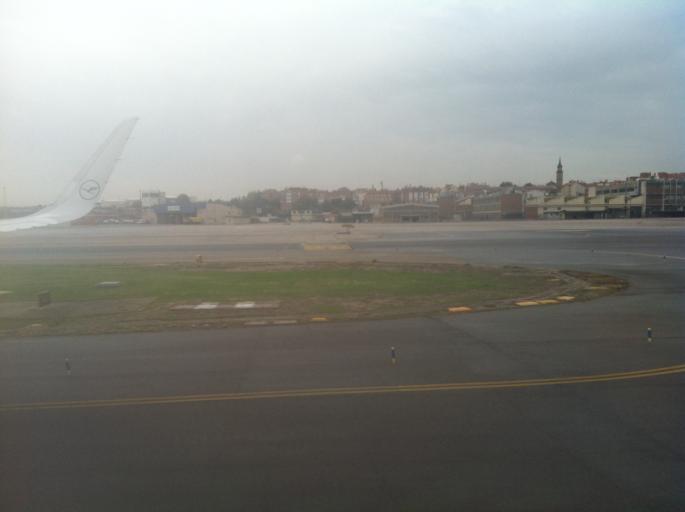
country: ES
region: Madrid
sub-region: Provincia de Madrid
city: Barajas de Madrid
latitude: 40.4763
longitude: -3.5701
